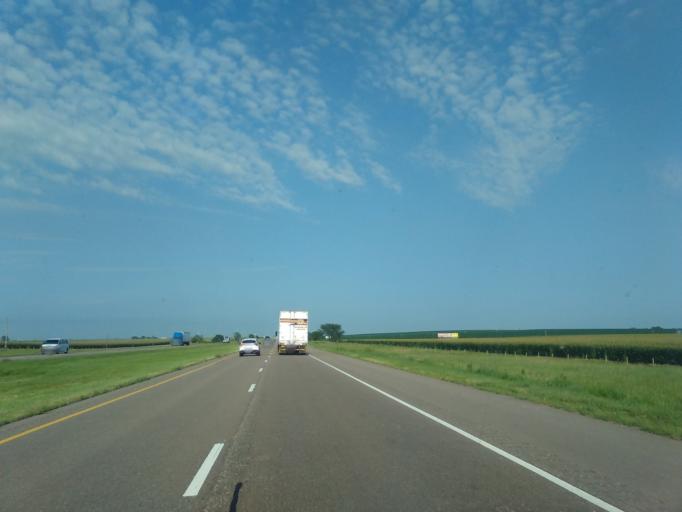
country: US
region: Nebraska
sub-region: York County
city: York
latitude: 40.8211
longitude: -97.6617
